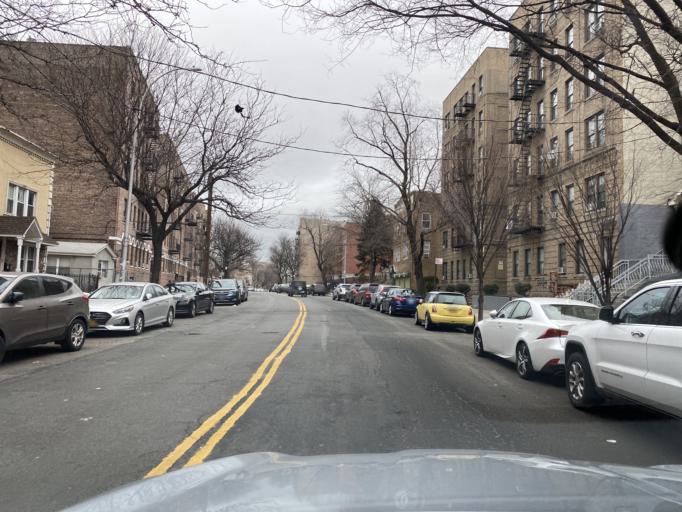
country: US
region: New York
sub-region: New York County
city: Inwood
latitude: 40.8708
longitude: -73.9025
